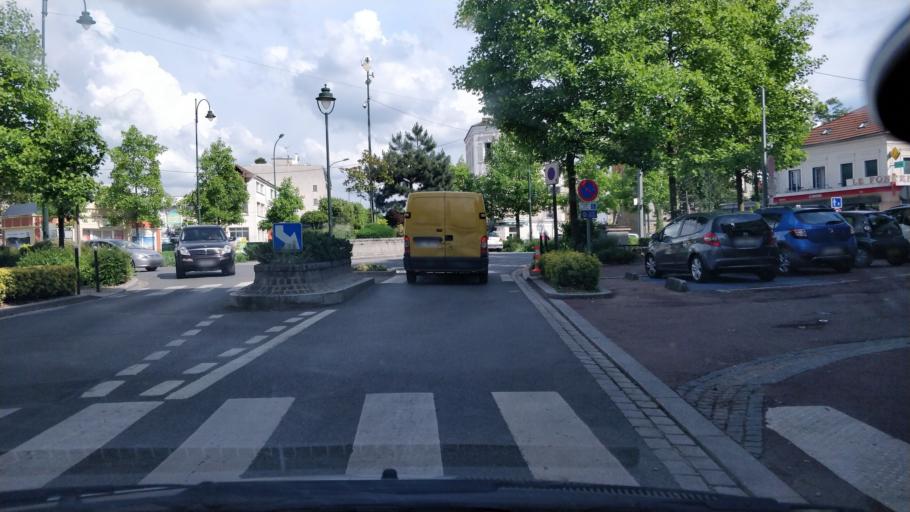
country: FR
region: Ile-de-France
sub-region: Departement de Seine-Saint-Denis
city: Le Raincy
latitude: 48.8995
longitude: 2.5170
